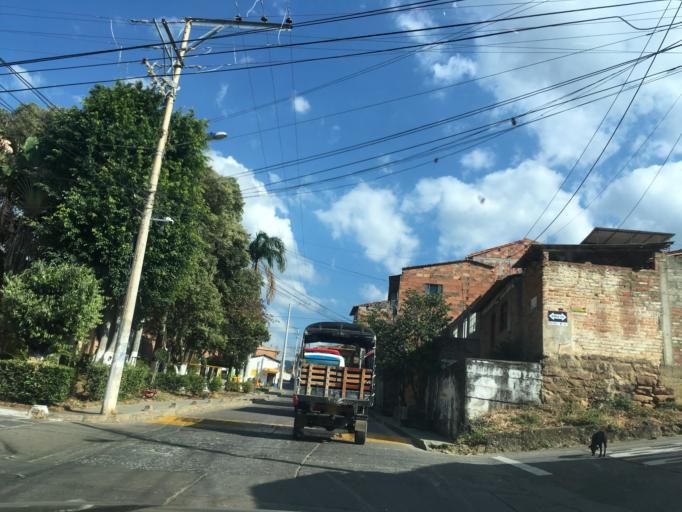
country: CO
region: Santander
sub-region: San Gil
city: San Gil
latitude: 6.5603
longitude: -73.1389
